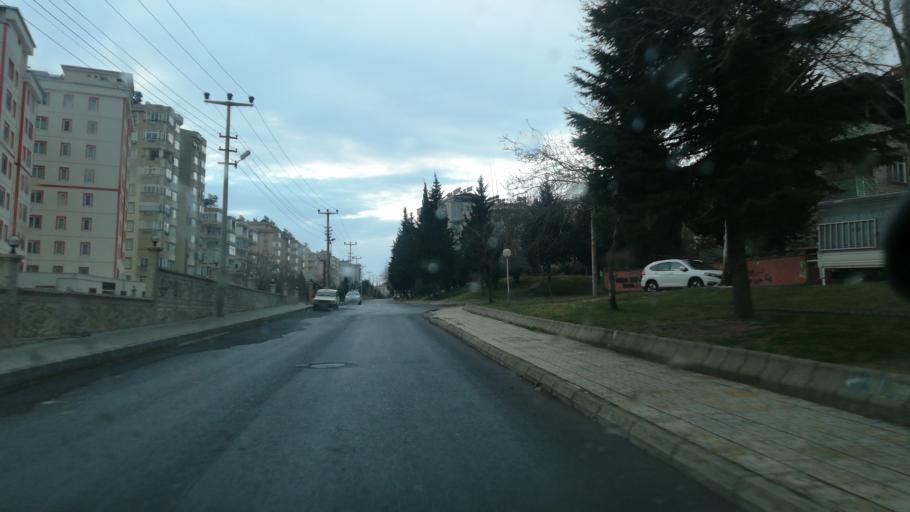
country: TR
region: Kahramanmaras
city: Kahramanmaras
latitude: 37.5878
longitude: 36.8962
